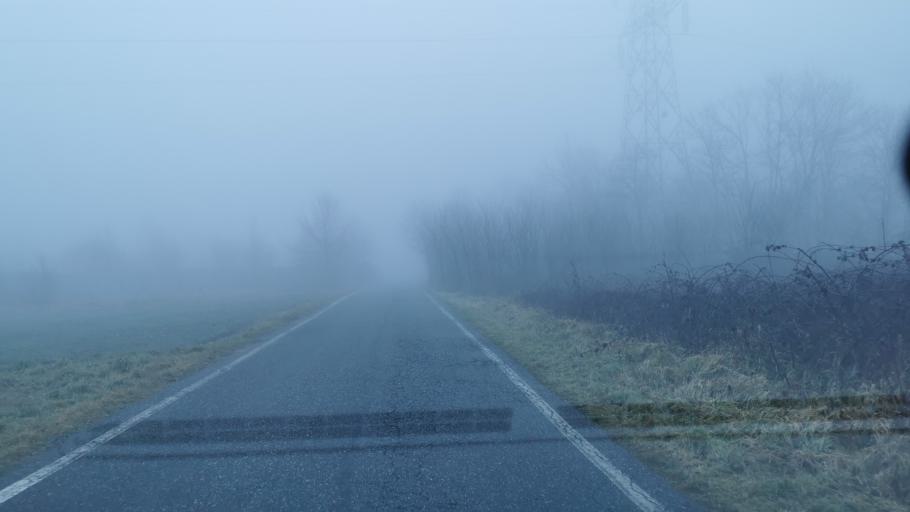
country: IT
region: Piedmont
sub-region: Provincia di Torino
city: Volpiano
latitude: 45.1927
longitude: 7.7624
